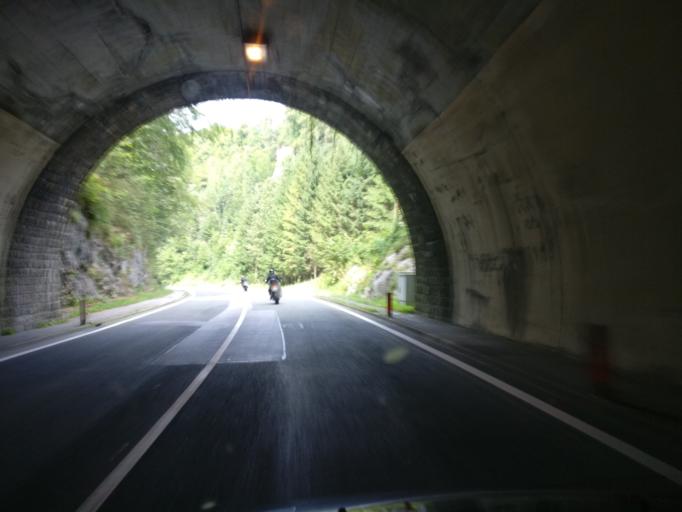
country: AT
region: Salzburg
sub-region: Politischer Bezirk Hallein
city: Scheffau am Tennengebirge
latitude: 47.5766
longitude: 13.1947
